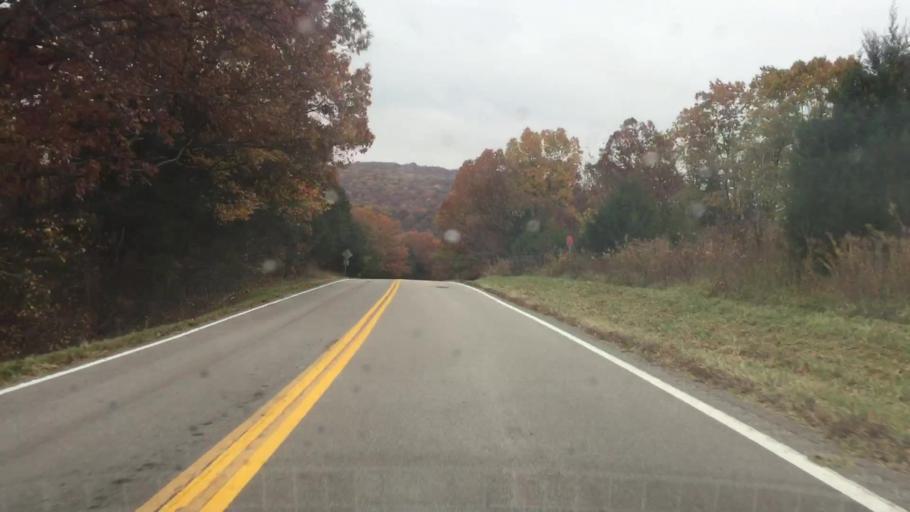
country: US
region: Missouri
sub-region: Gasconade County
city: Hermann
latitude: 38.7092
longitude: -91.6319
